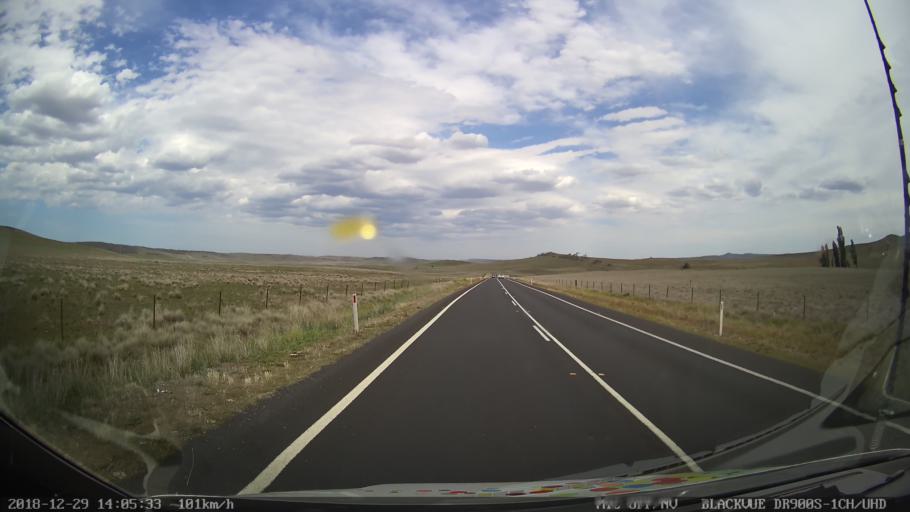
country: AU
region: New South Wales
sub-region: Cooma-Monaro
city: Cooma
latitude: -36.3320
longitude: 149.1927
